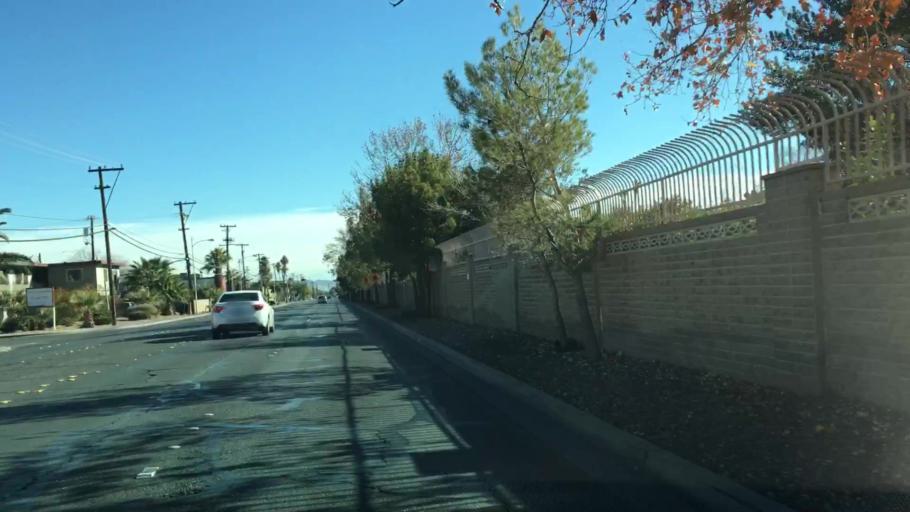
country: US
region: Nevada
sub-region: Clark County
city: Winchester
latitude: 36.1404
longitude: -115.1476
